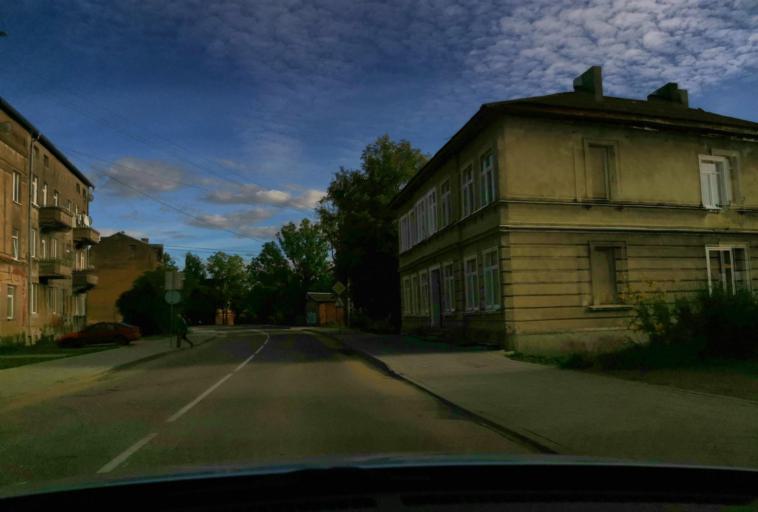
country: RU
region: Kaliningrad
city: Chernyakhovsk
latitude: 54.6263
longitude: 21.8136
